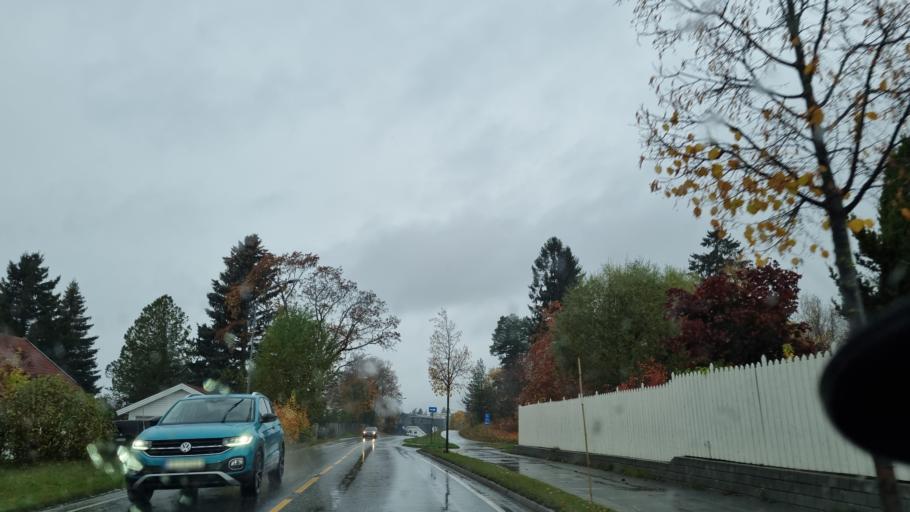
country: NO
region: Hedmark
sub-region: Hamar
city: Hamar
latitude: 60.8051
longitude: 11.1265
